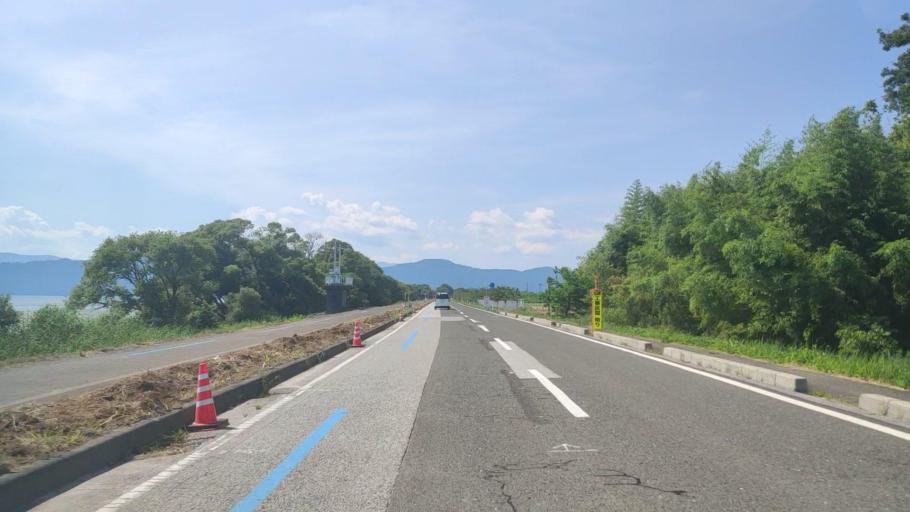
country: JP
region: Shiga Prefecture
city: Nagahama
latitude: 35.4368
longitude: 136.1942
